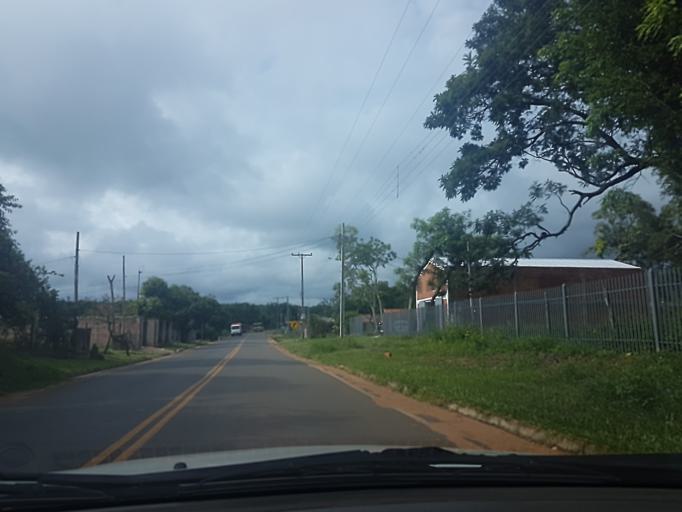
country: PY
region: Central
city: Limpio
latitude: -25.2325
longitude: -57.4493
